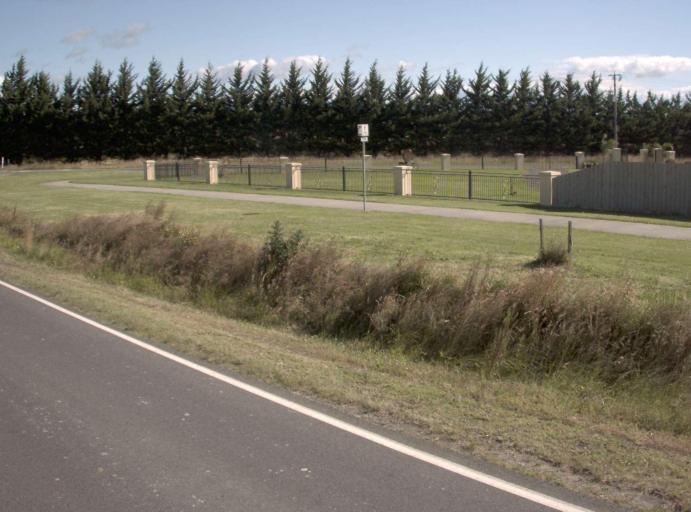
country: AU
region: Victoria
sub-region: Latrobe
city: Traralgon
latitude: -38.1828
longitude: 146.5006
